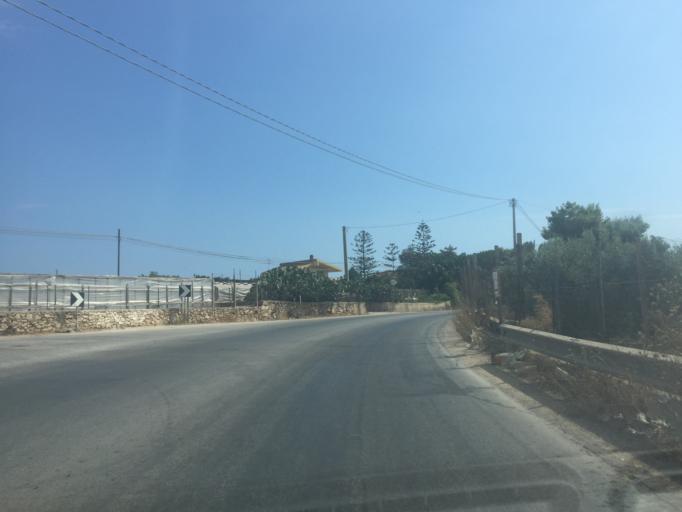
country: IT
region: Sicily
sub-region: Ragusa
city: Santa Croce Camerina
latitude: 36.8121
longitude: 14.5191
